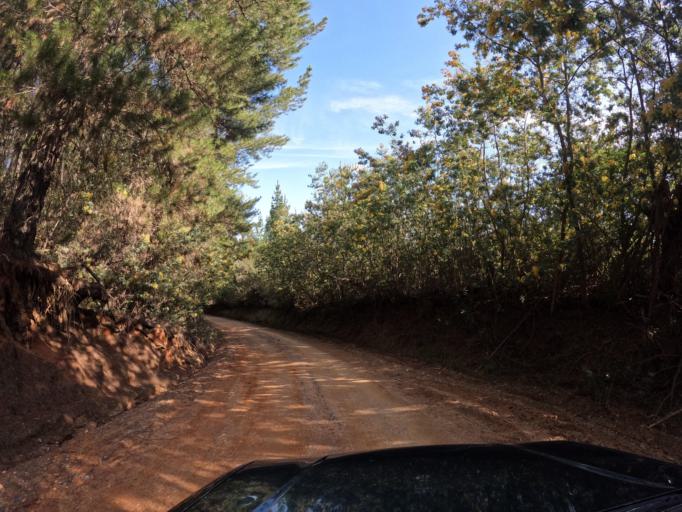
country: CL
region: Biobio
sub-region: Provincia de Biobio
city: La Laja
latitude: -37.1280
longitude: -72.7349
